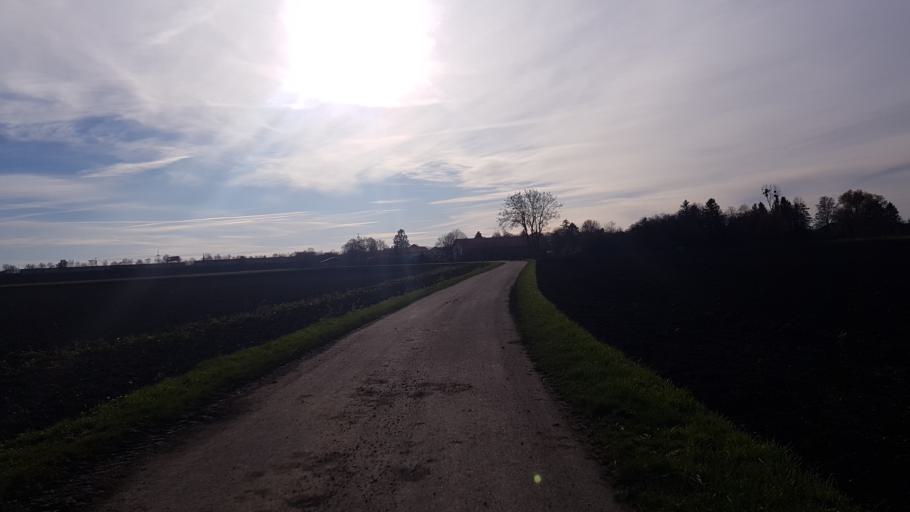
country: DE
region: Bavaria
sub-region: Upper Bavaria
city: Oberschleissheim
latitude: 48.2308
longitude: 11.5313
